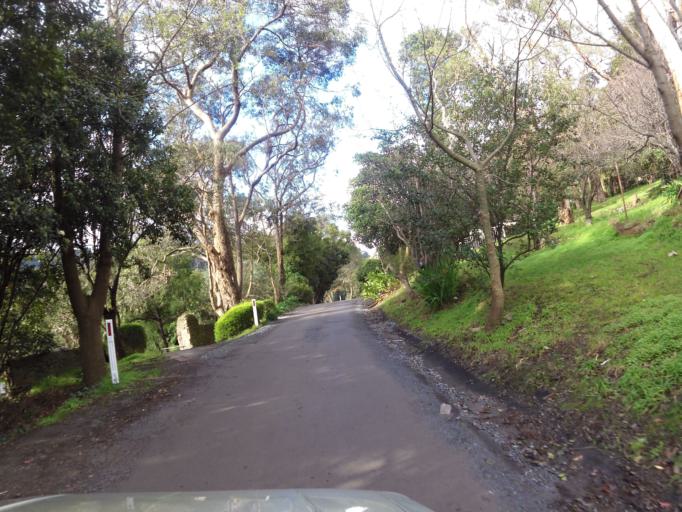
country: AU
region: Victoria
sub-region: Yarra Ranges
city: Tremont
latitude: -37.9004
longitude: 145.3172
